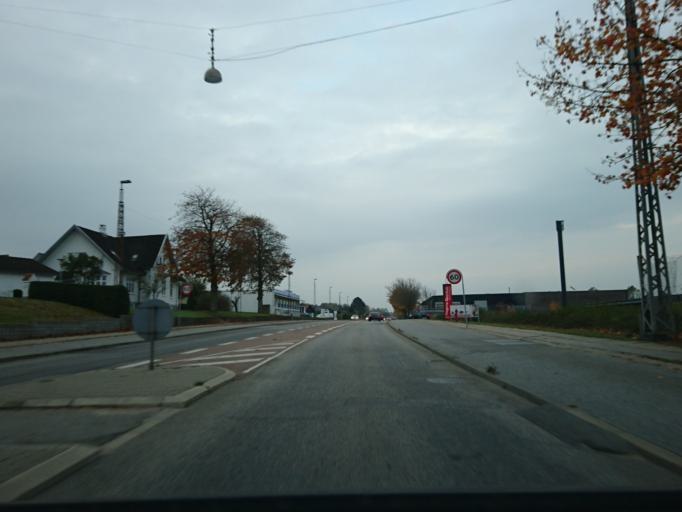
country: DK
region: North Denmark
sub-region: Alborg Kommune
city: Aalborg
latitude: 57.0228
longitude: 9.9267
